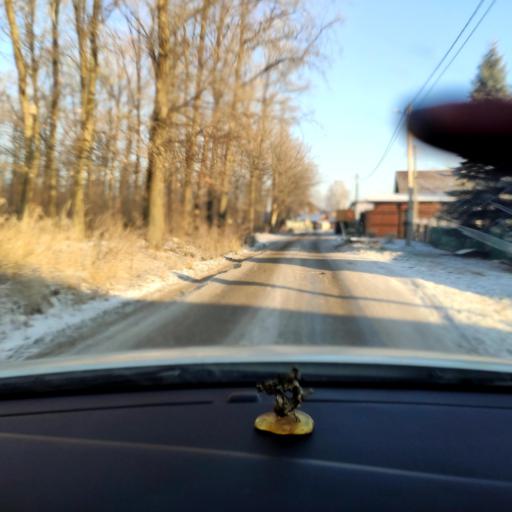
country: RU
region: Tatarstan
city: Stolbishchi
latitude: 55.6743
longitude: 49.1111
